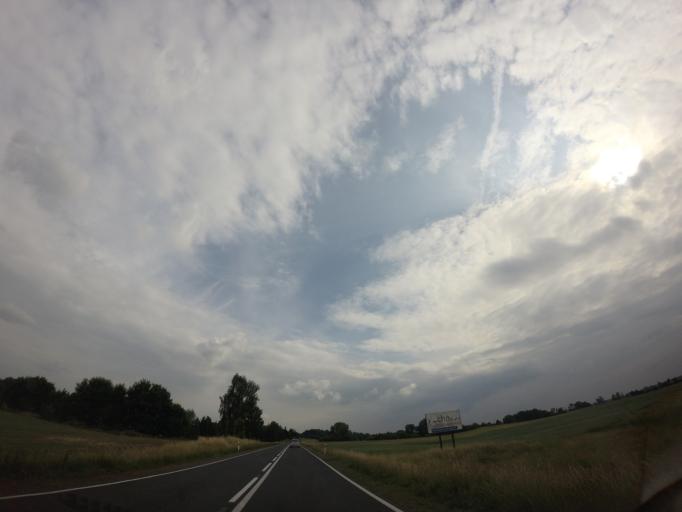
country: PL
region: West Pomeranian Voivodeship
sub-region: Powiat szczecinecki
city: Szczecinek
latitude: 53.6676
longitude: 16.6777
